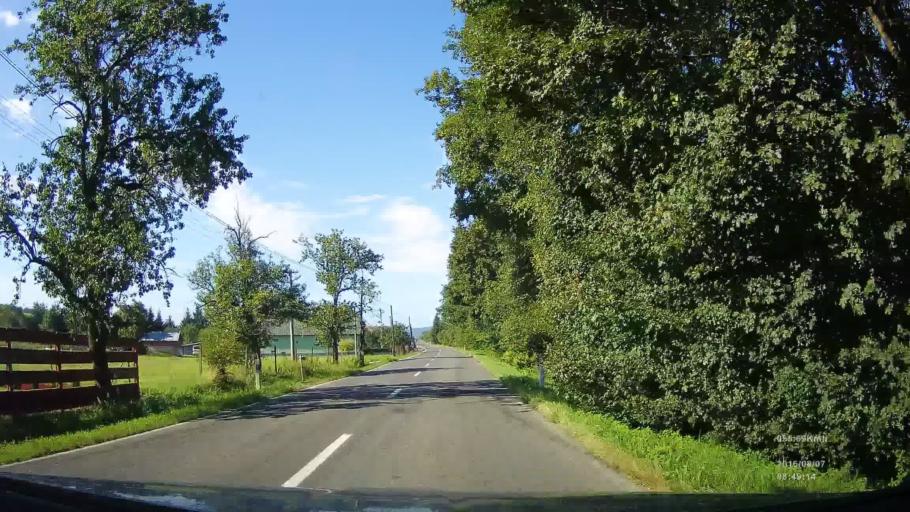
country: SK
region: Presovsky
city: Stropkov
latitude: 49.2543
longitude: 21.6903
